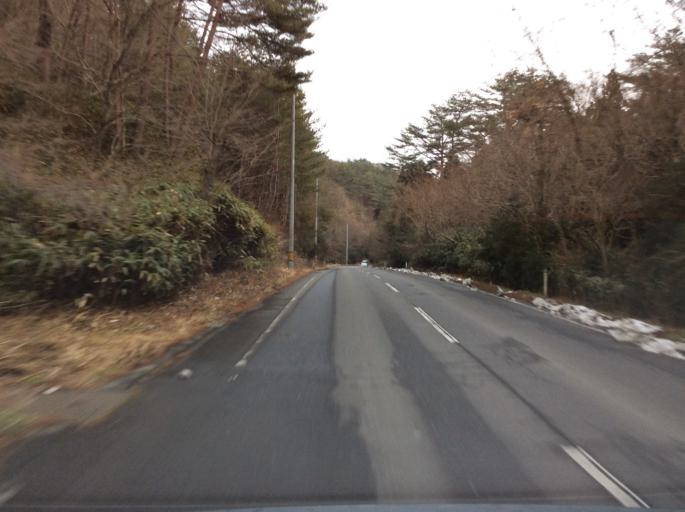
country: JP
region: Fukushima
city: Iwaki
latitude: 37.1431
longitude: 140.9445
